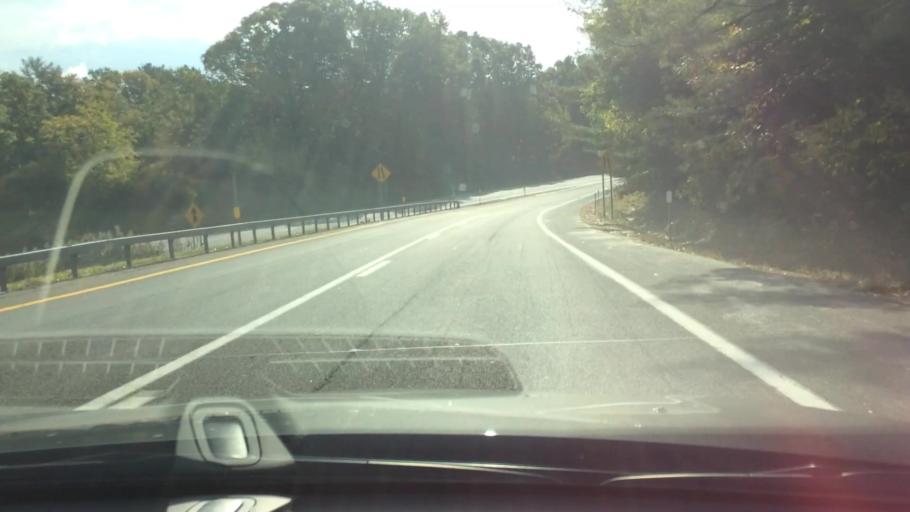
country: US
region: New York
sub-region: Saratoga County
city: Saratoga Springs
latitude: 43.0952
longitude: -73.7529
